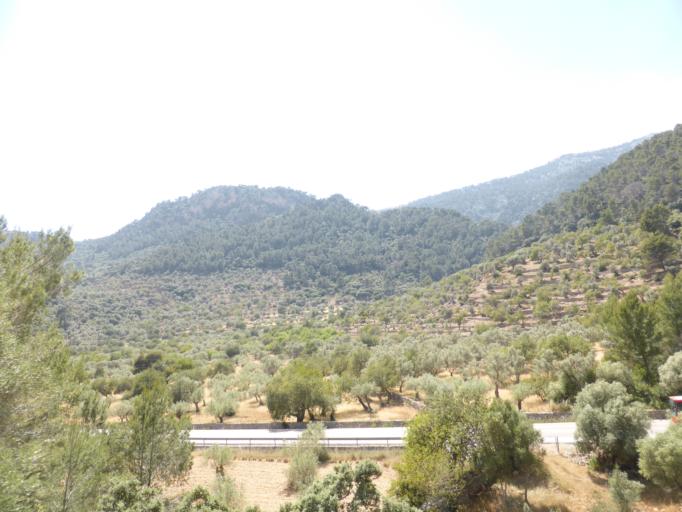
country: ES
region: Balearic Islands
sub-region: Illes Balears
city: Bunyola
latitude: 39.7114
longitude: 2.6904
